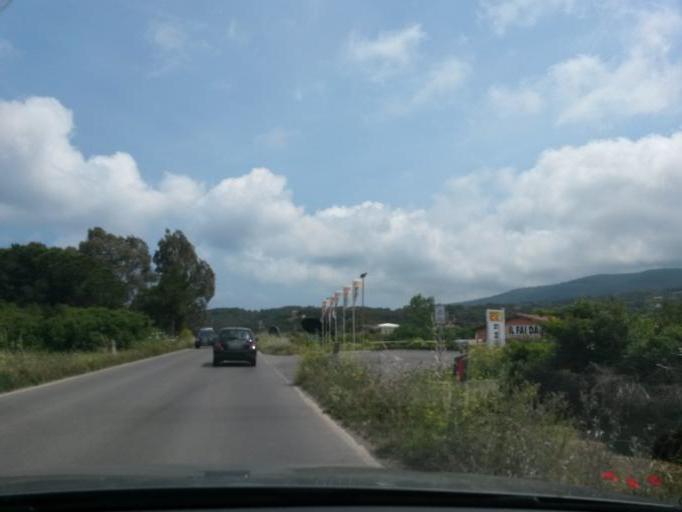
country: IT
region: Tuscany
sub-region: Provincia di Livorno
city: Capoliveri
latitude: 42.7592
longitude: 10.3735
